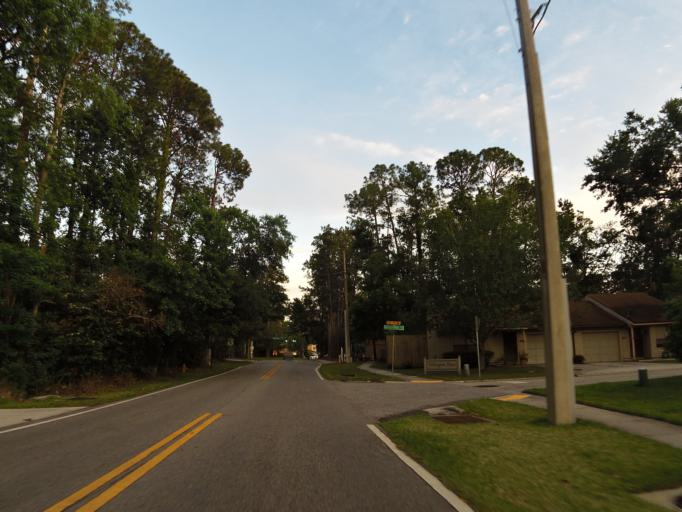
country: US
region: Florida
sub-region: Duval County
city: Jacksonville
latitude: 30.2754
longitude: -81.5914
